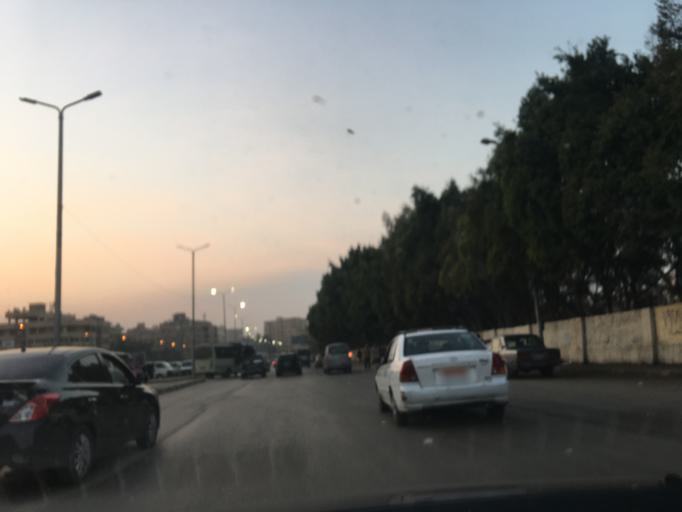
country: EG
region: Al Jizah
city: Al Jizah
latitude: 29.9902
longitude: 31.1340
